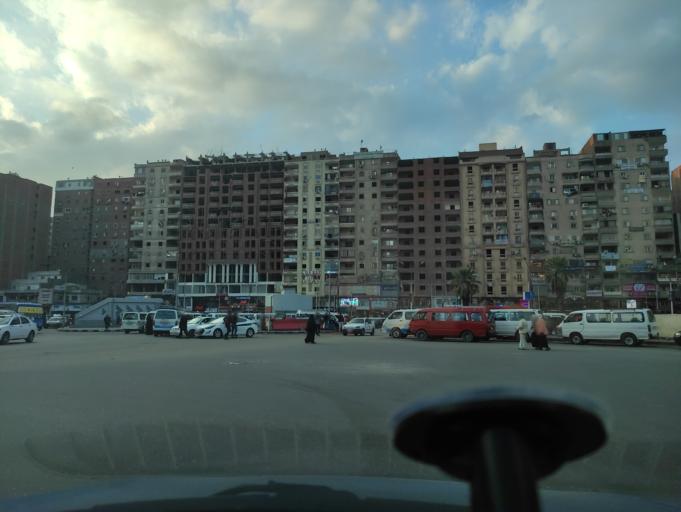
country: EG
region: Muhafazat al Qalyubiyah
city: Al Khankah
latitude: 30.1185
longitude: 31.3407
